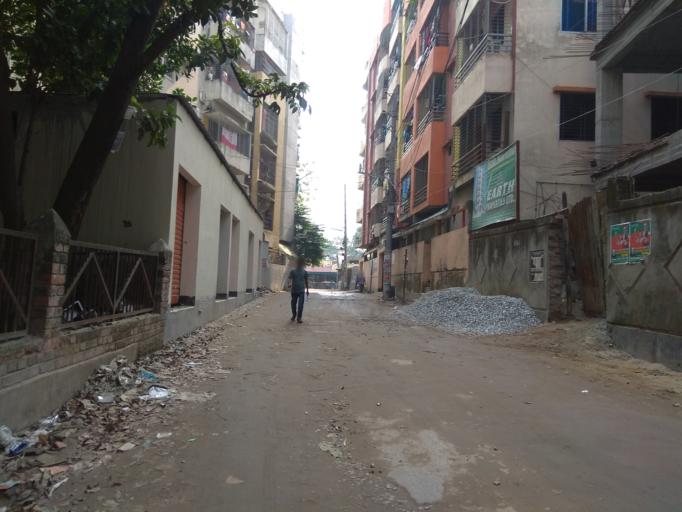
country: BD
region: Dhaka
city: Tungi
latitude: 23.8620
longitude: 90.3931
